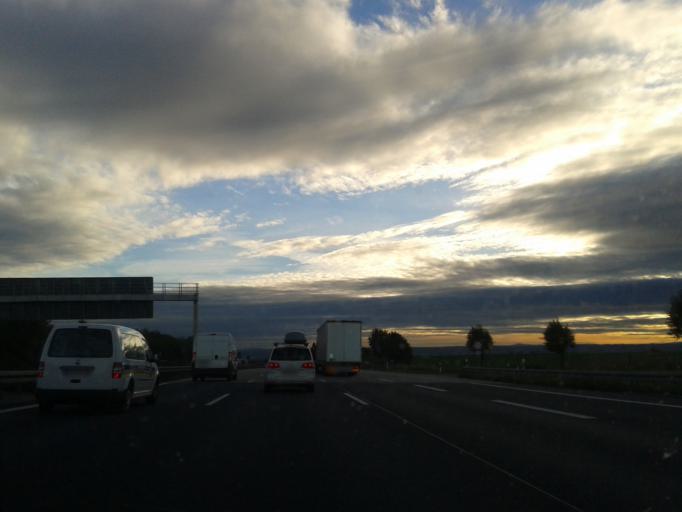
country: DE
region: Saxony
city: Radebeul
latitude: 51.0663
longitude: 13.6210
